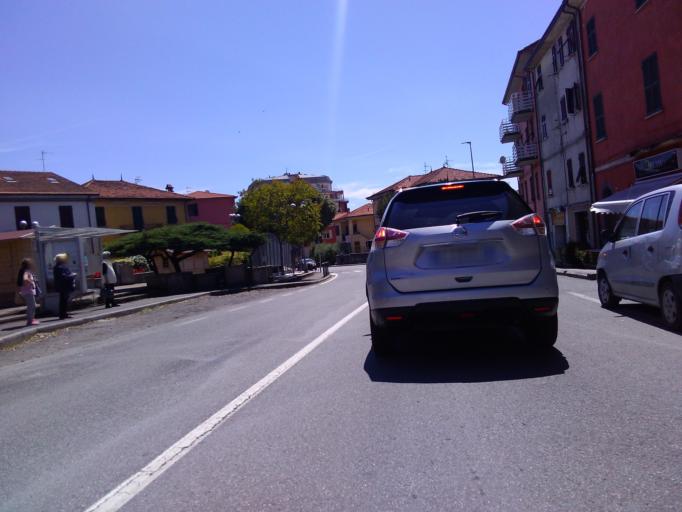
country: IT
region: Tuscany
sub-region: Provincia di Massa-Carrara
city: Albiano Magra
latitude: 44.1643
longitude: 9.9162
